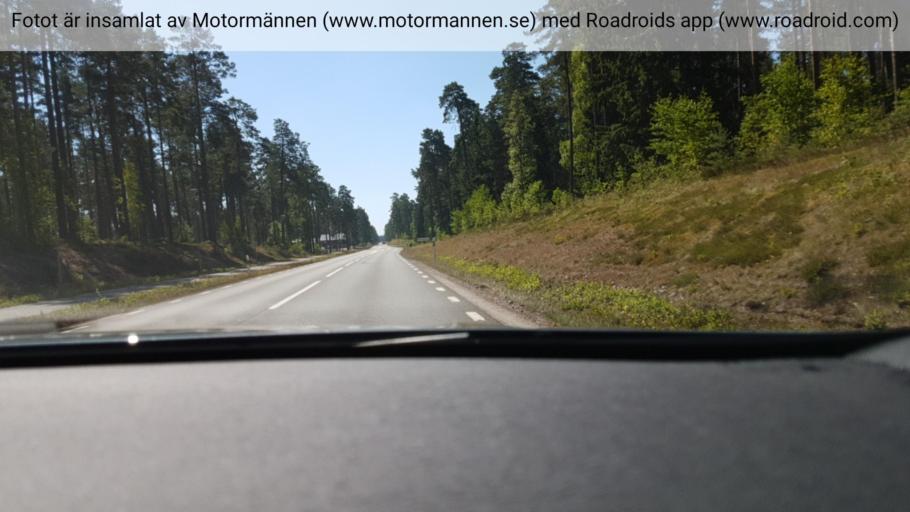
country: SE
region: Joenkoeping
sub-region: Mullsjo Kommun
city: Mullsjoe
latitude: 57.8955
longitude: 13.8415
